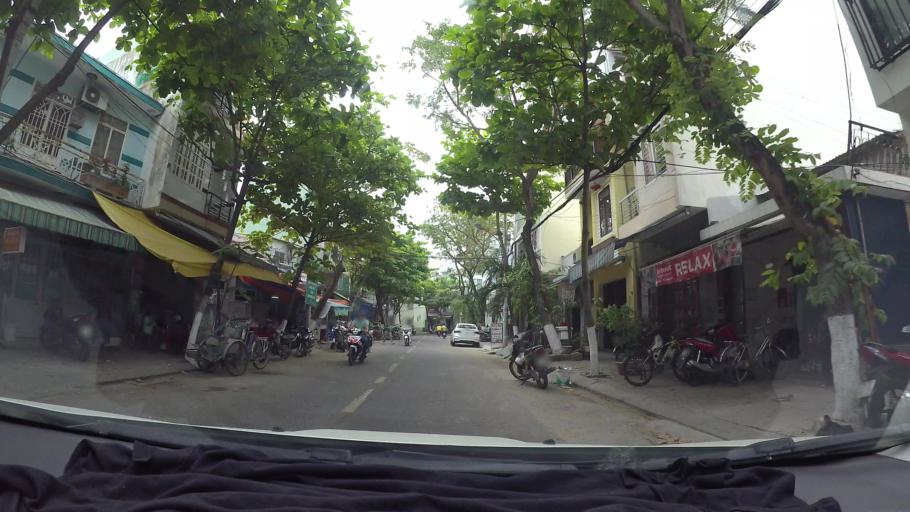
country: VN
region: Da Nang
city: Da Nang
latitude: 16.0842
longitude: 108.2156
